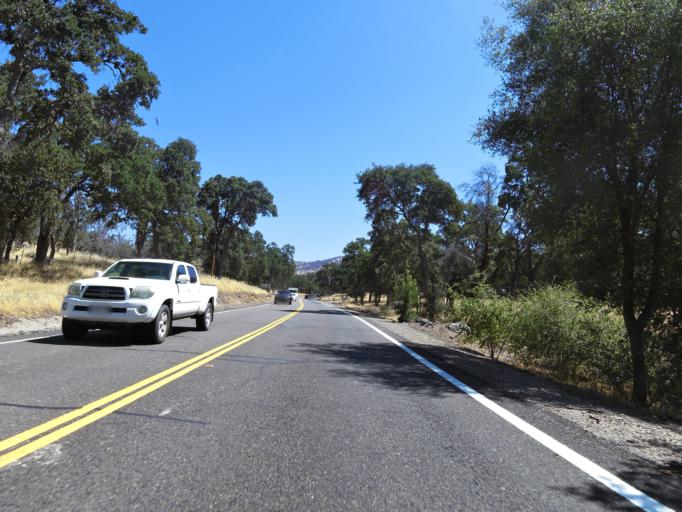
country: US
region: California
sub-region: Mariposa County
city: Mariposa
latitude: 37.4389
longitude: -120.0858
